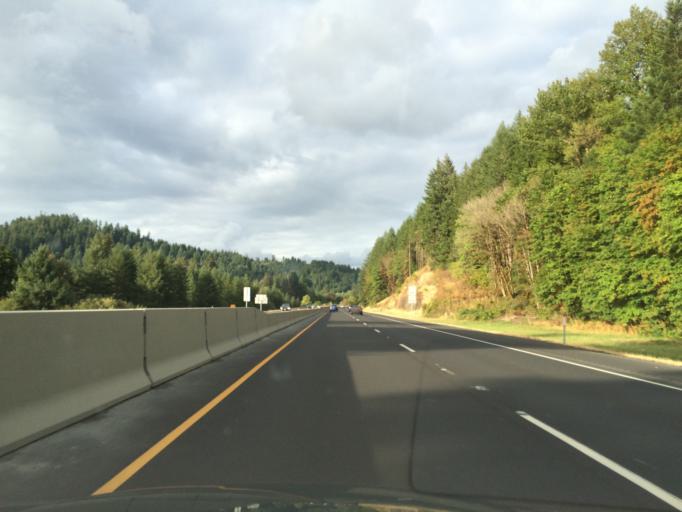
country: US
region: Oregon
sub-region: Douglas County
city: Drain
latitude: 43.7296
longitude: -123.2010
